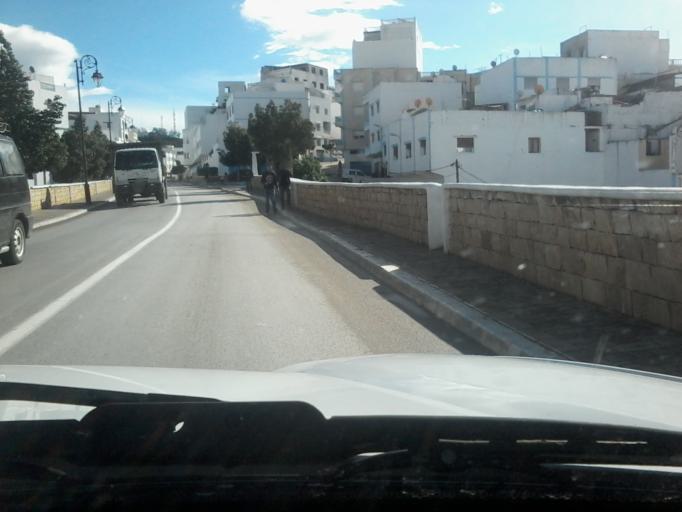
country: MA
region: Tanger-Tetouan
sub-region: Tetouan
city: Martil
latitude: 35.6805
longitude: -5.3267
